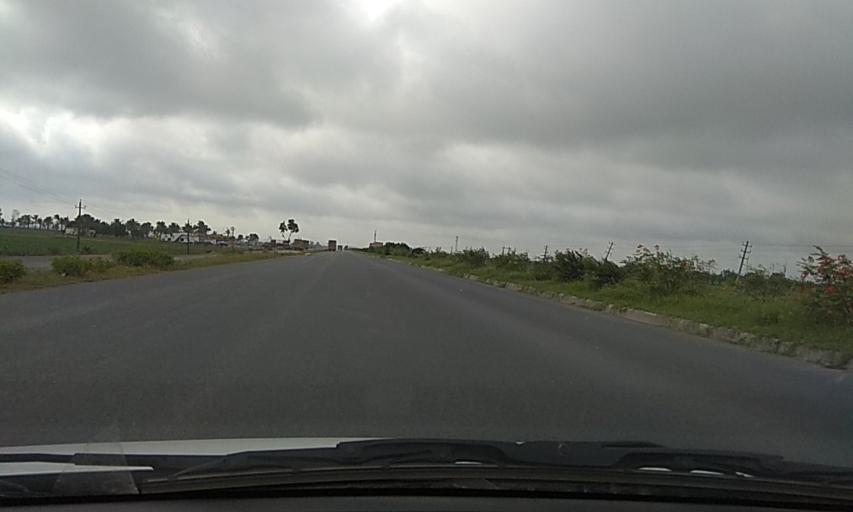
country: IN
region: Karnataka
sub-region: Haveri
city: Savanur
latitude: 14.8898
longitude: 75.3006
